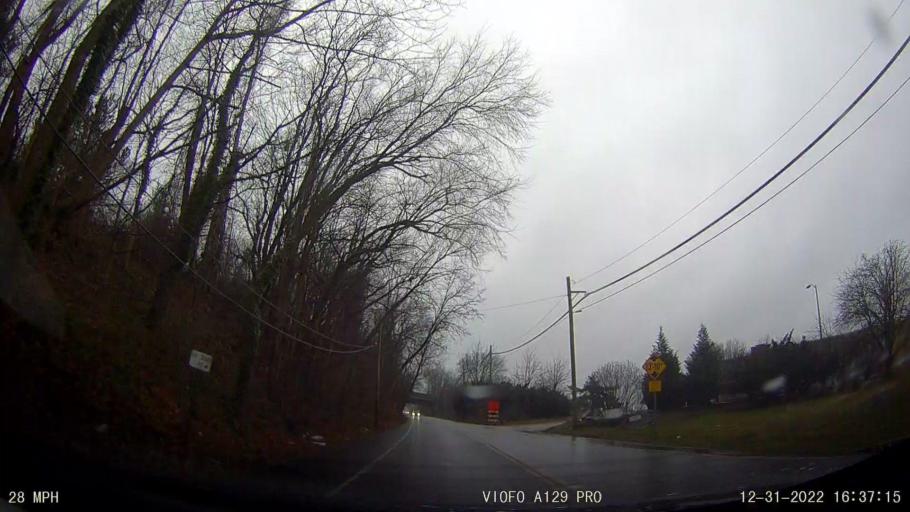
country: US
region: Pennsylvania
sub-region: Montgomery County
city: King of Prussia
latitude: 40.0799
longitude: -75.3754
